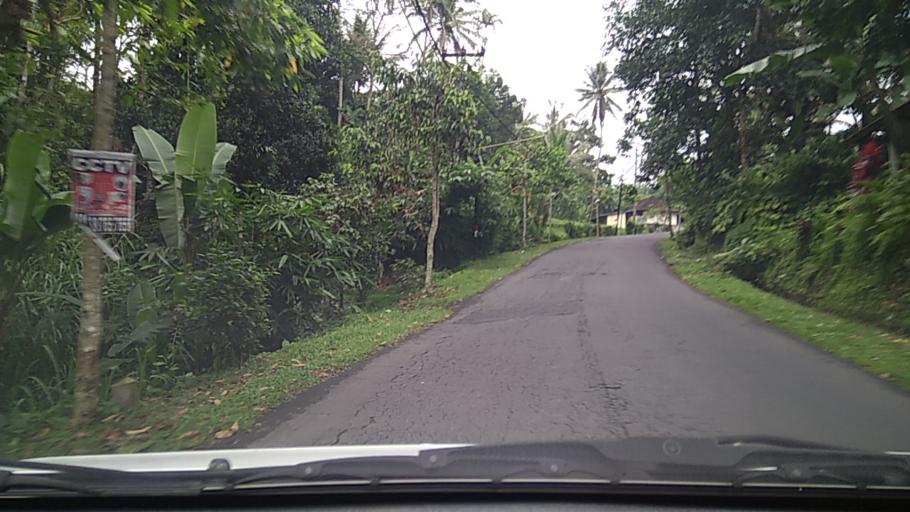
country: ID
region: Bali
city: Banjar Manukayaanyar
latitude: -8.4197
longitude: 115.3020
